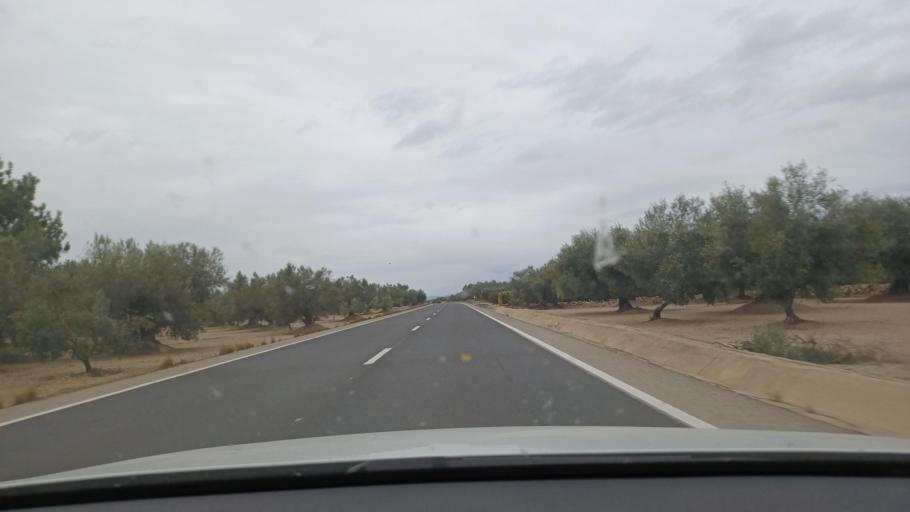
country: ES
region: Catalonia
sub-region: Provincia de Tarragona
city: Ulldecona
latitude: 40.6592
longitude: 0.4133
